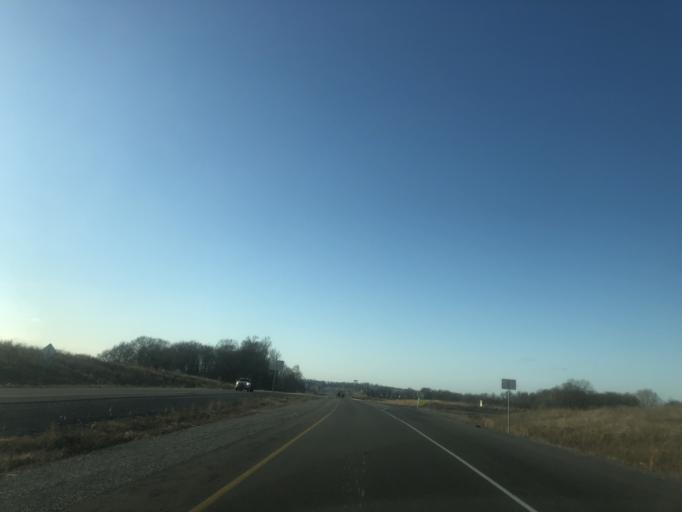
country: US
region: Tennessee
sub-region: Sumner County
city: Portland
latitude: 36.6217
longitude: -86.5543
